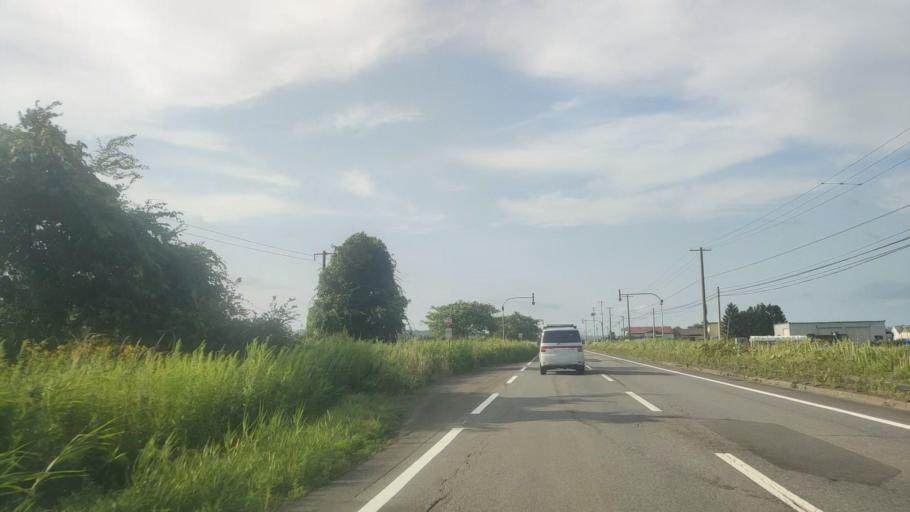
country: JP
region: Hokkaido
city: Chitose
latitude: 42.9573
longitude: 141.7985
